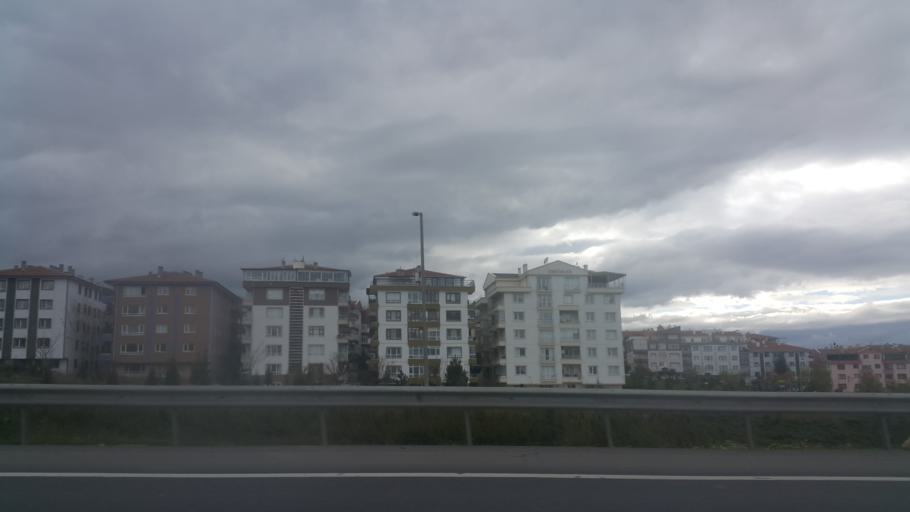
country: TR
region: Ankara
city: Etimesgut
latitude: 39.9509
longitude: 32.6230
